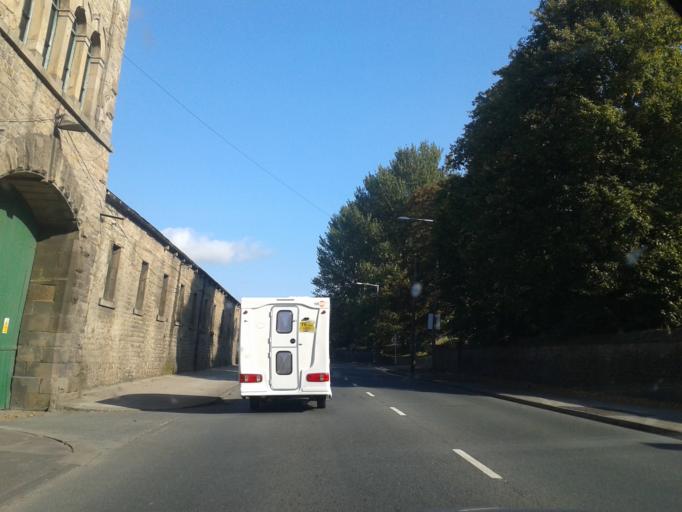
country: GB
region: England
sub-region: Lancashire
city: Lancaster
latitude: 54.0601
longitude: -2.7892
